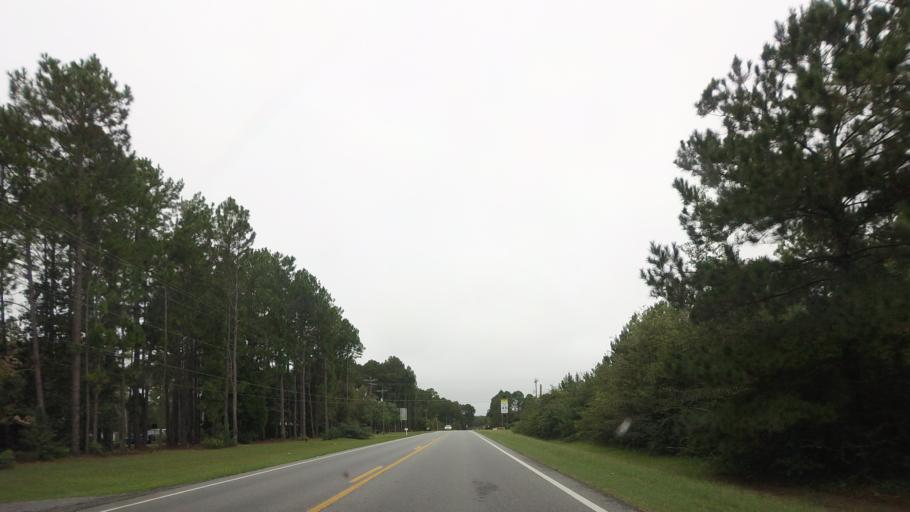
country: US
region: Georgia
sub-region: Berrien County
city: Nashville
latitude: 31.2326
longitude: -83.2466
